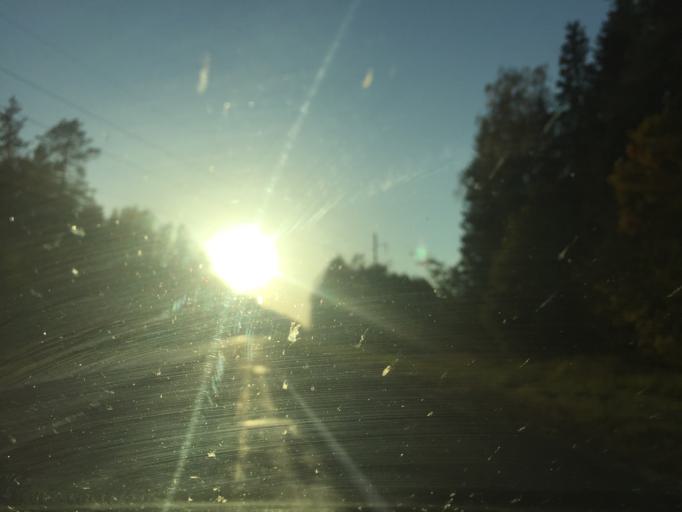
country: BY
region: Mogilev
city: Poselok Voskhod
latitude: 53.7762
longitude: 30.3903
